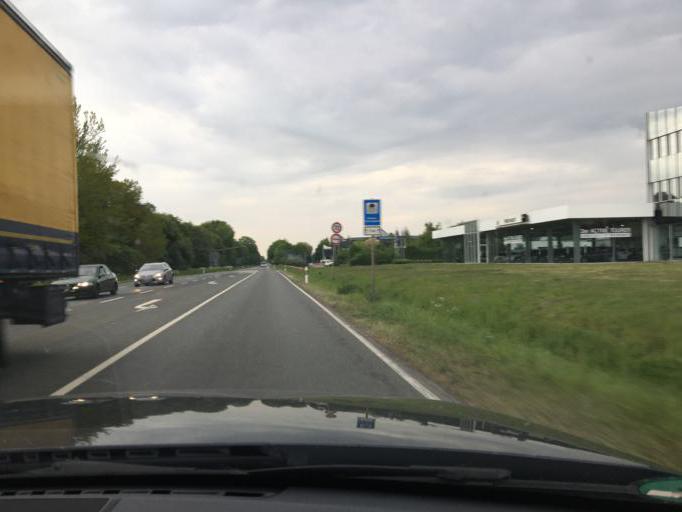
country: DE
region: North Rhine-Westphalia
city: Emsdetten
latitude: 52.1446
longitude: 7.5636
